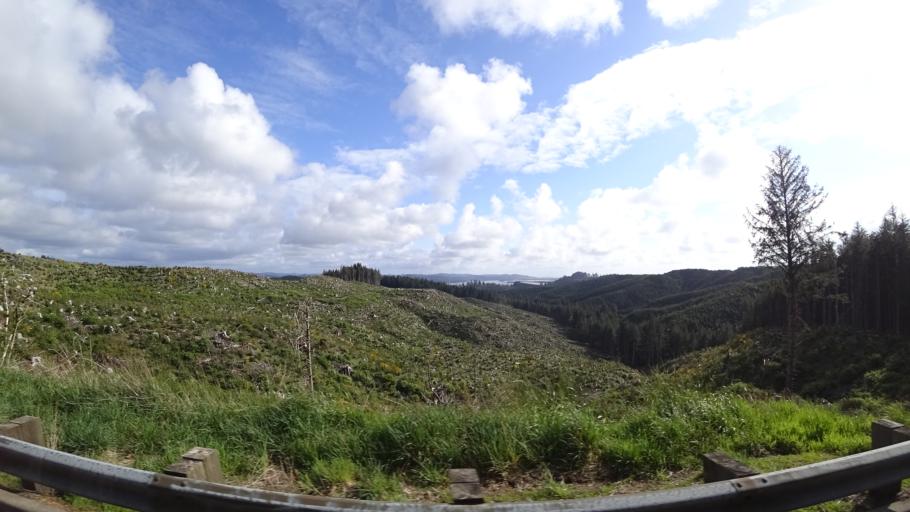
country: US
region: Oregon
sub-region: Douglas County
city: Reedsport
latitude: 43.7705
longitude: -124.1395
